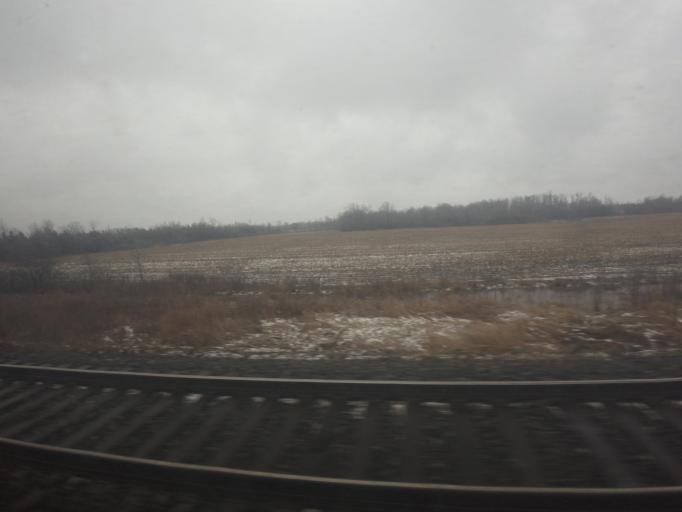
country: CA
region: Ontario
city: Deseronto
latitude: 44.2161
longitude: -77.1697
